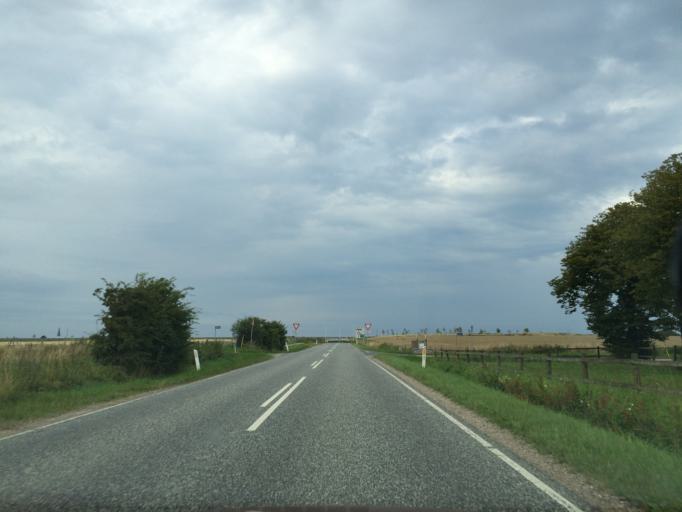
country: DK
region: South Denmark
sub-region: Sonderborg Kommune
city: Broager
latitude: 54.9314
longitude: 9.6907
